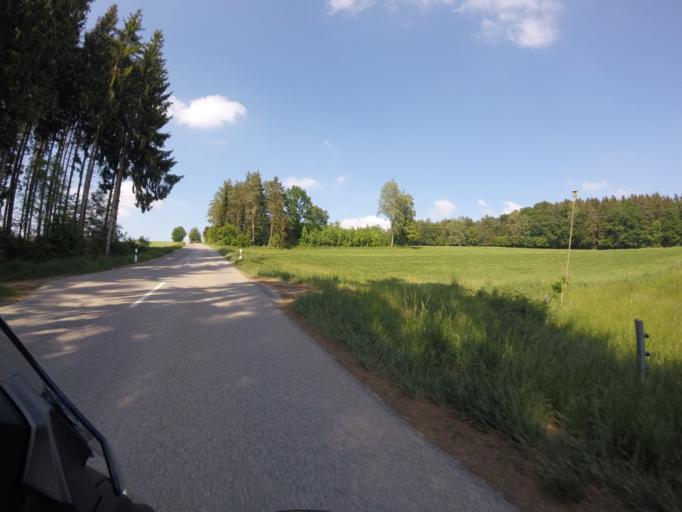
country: DE
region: Bavaria
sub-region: Upper Bavaria
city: Scheyern
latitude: 48.4810
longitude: 11.4524
